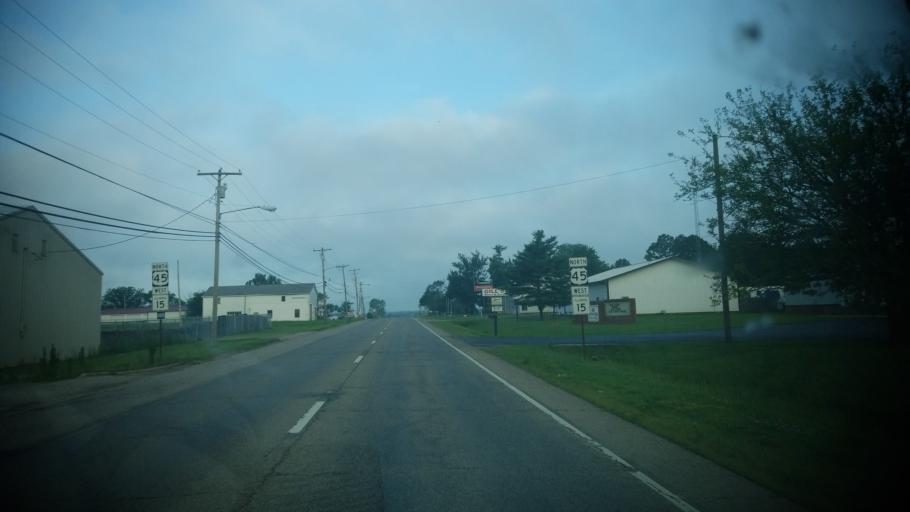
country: US
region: Illinois
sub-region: Wayne County
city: Fairfield
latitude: 38.3797
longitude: -88.3838
